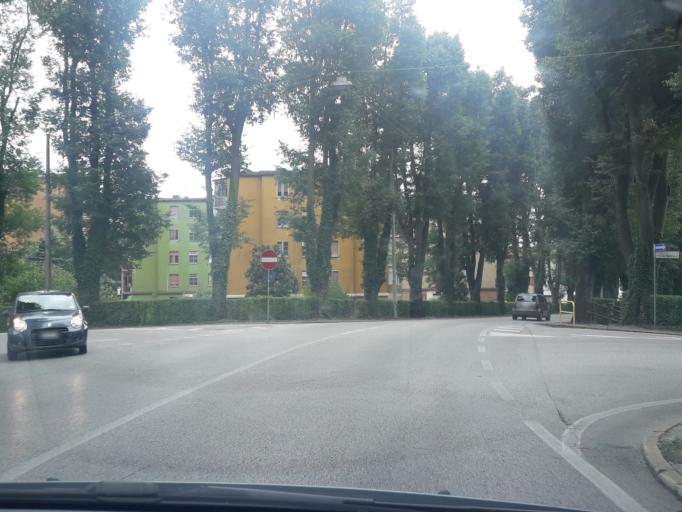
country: IT
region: Friuli Venezia Giulia
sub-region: Provincia di Udine
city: Udine
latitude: 46.0557
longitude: 13.2467
